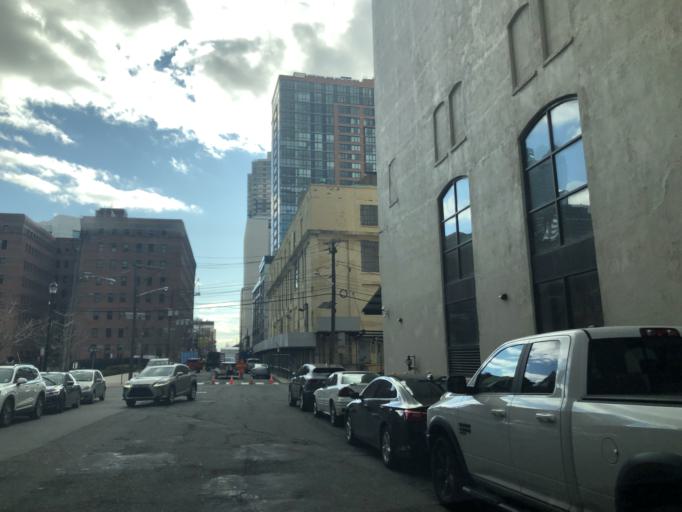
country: US
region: New Jersey
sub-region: Hudson County
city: Hoboken
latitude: 40.7216
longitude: -74.0382
